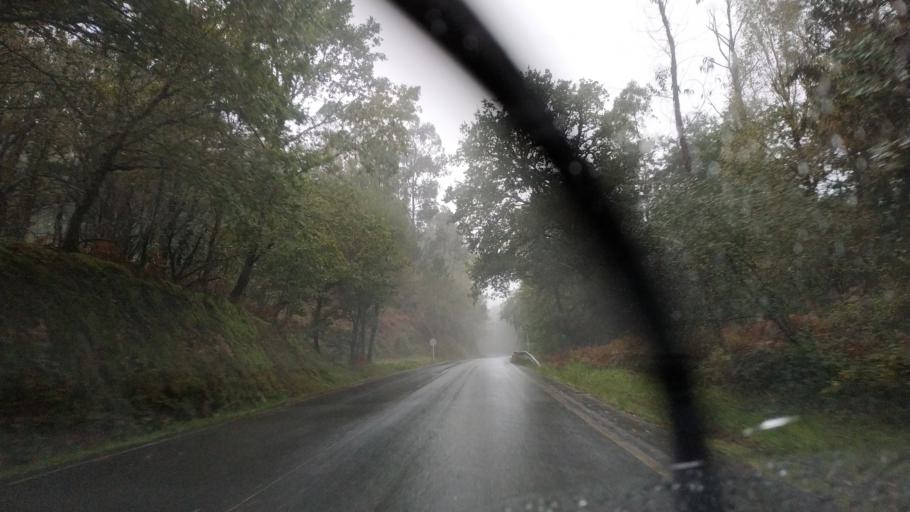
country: ES
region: Galicia
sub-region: Provincia da Coruna
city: Negreira
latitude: 42.9096
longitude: -8.7498
